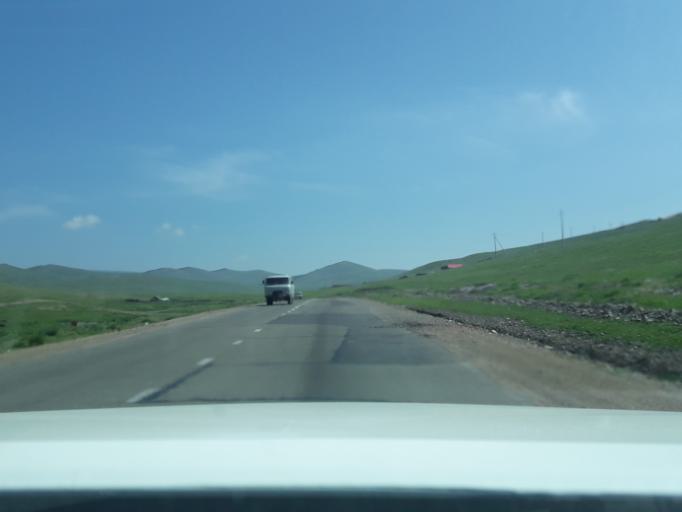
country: MN
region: Central Aimak
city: Zuunmod
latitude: 47.7385
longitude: 106.8397
